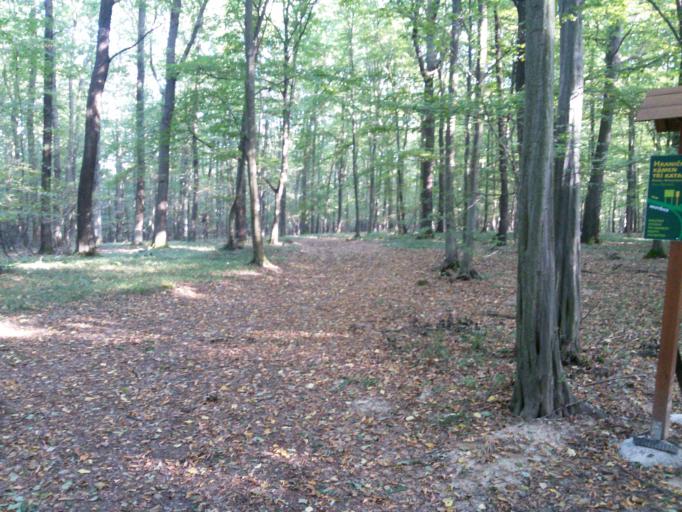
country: CZ
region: Zlin
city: Bilovice
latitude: 49.0804
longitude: 17.5707
